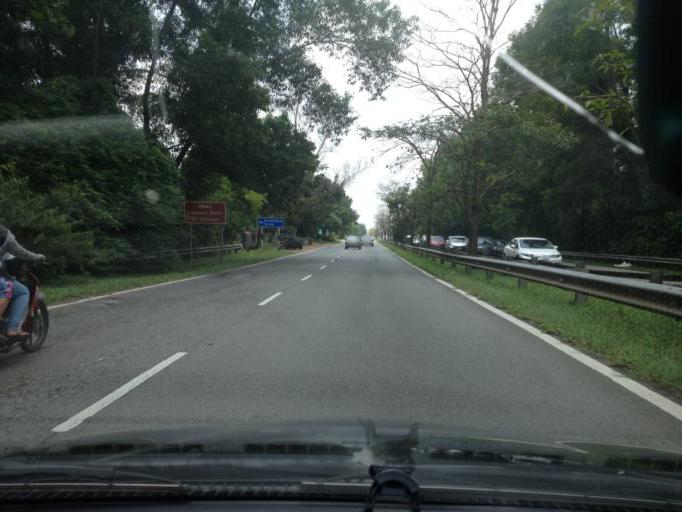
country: MY
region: Kedah
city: Sungai Petani
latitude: 5.6394
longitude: 100.5394
